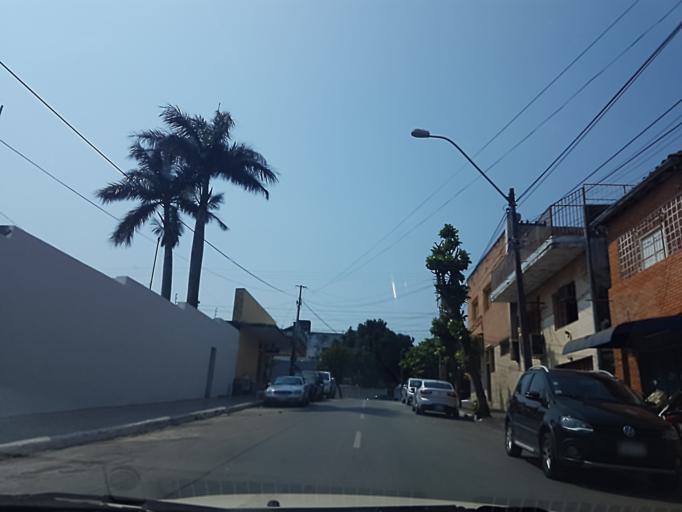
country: PY
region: Asuncion
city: Asuncion
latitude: -25.2989
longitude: -57.6358
